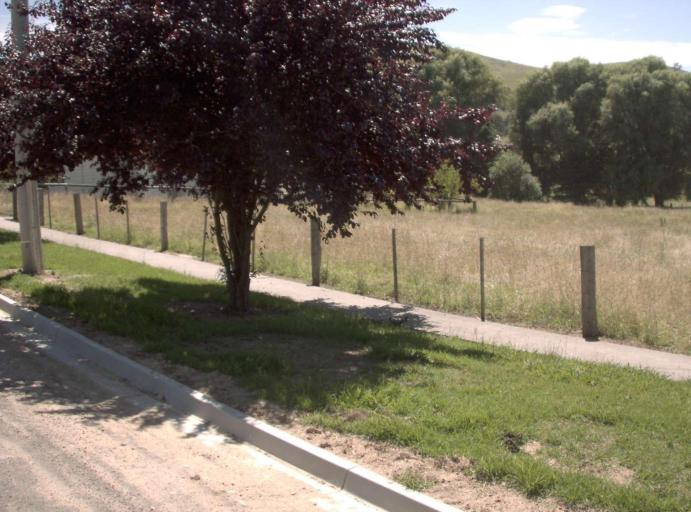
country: AU
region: Victoria
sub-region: East Gippsland
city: Lakes Entrance
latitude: -37.5004
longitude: 148.1717
